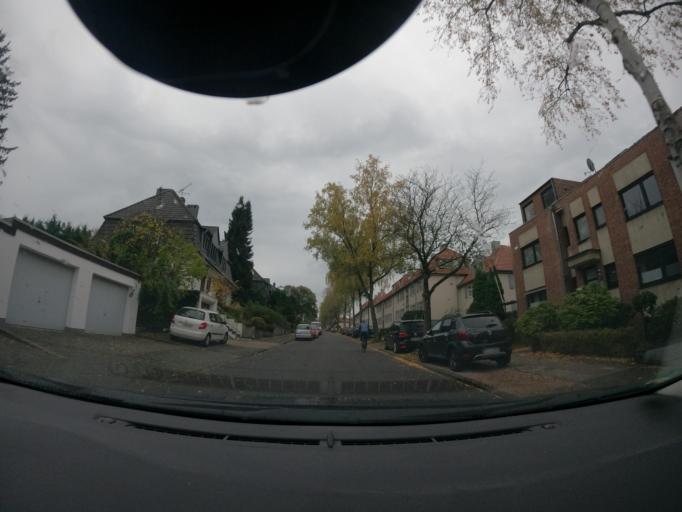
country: DE
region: North Rhine-Westphalia
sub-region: Regierungsbezirk Koln
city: Aachen
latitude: 50.7572
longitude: 6.0984
